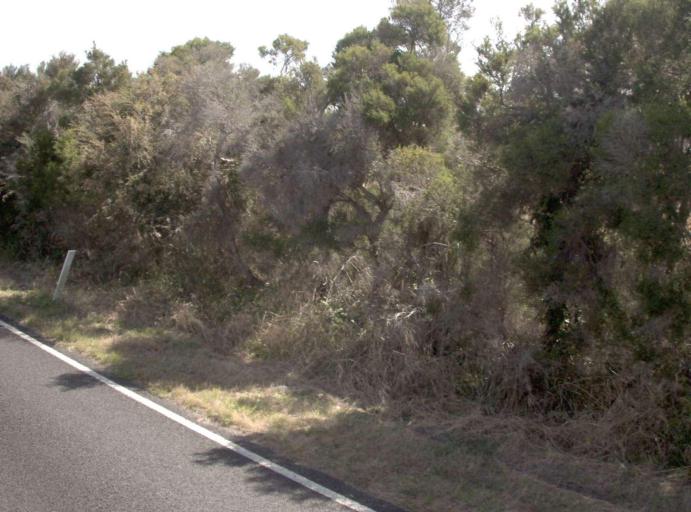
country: AU
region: Victoria
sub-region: Wellington
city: Sale
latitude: -38.3490
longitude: 147.1720
